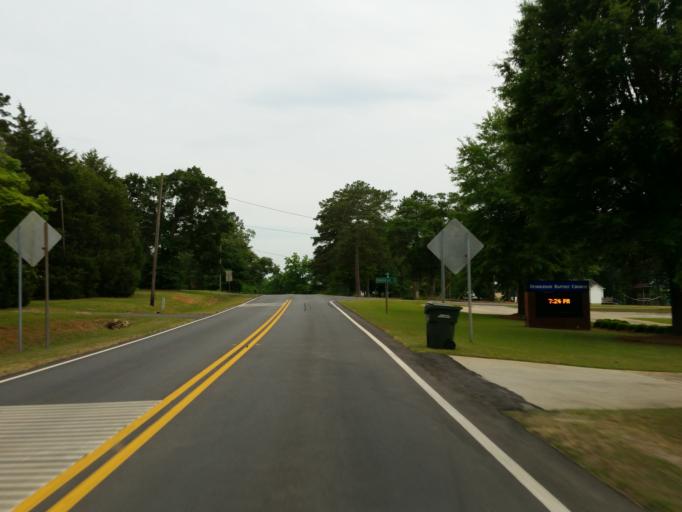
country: US
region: Georgia
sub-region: Dooly County
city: Unadilla
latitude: 32.3398
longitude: -83.7894
